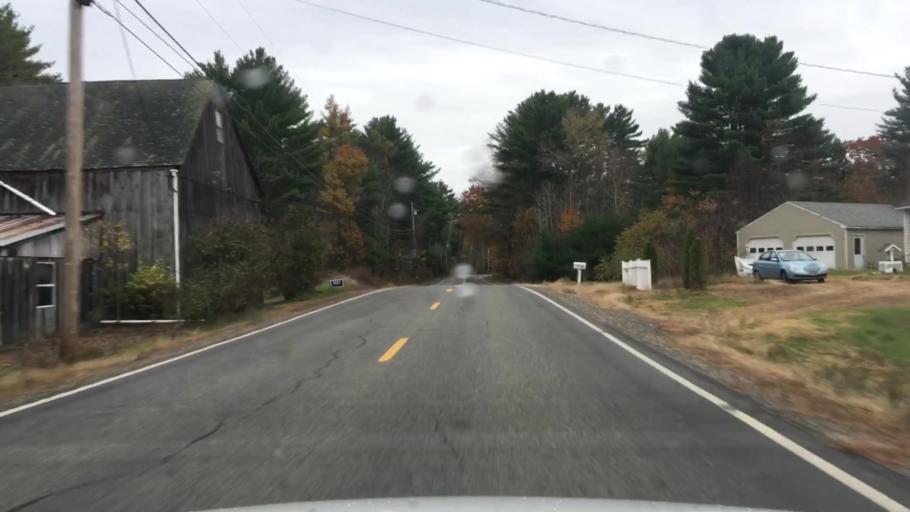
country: US
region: Maine
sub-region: Lincoln County
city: Jefferson
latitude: 44.1804
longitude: -69.4339
